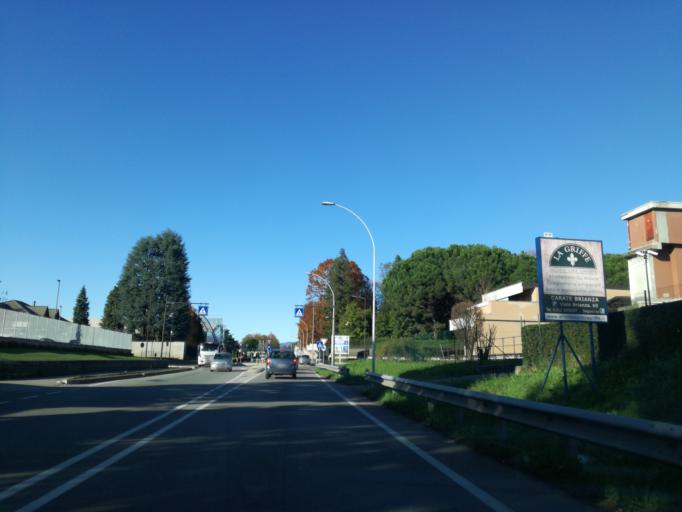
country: IT
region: Lombardy
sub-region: Provincia di Monza e Brianza
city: Sovico
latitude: 45.6515
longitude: 9.2575
